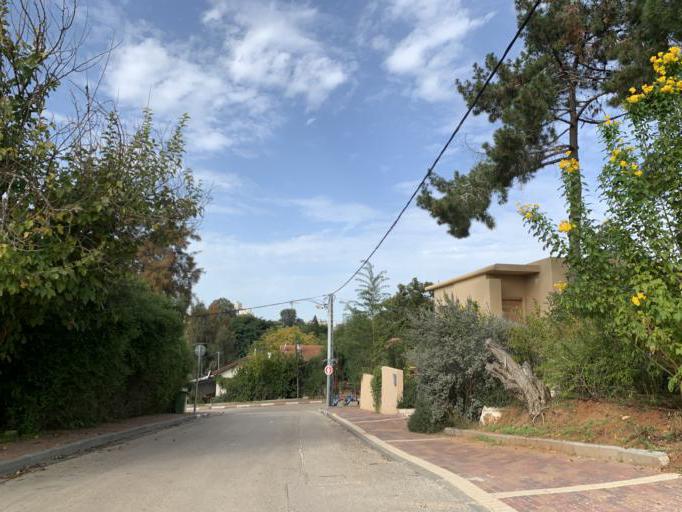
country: IL
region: Central District
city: Hod HaSharon
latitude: 32.1508
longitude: 34.9034
